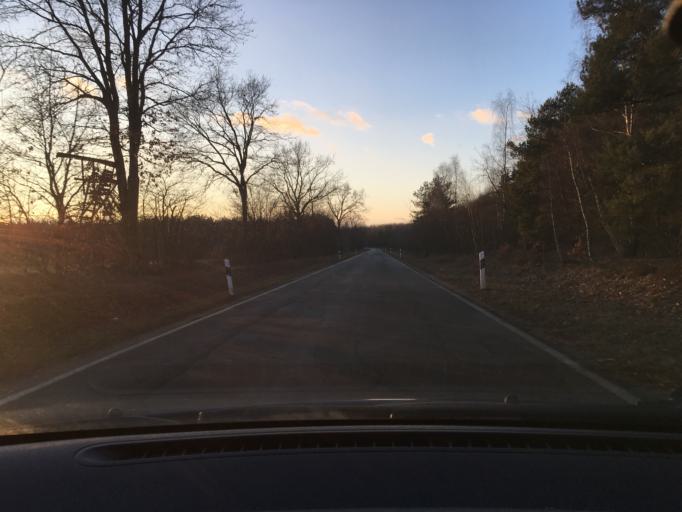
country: DE
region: Schleswig-Holstein
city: Brothen
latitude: 53.4849
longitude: 10.6817
